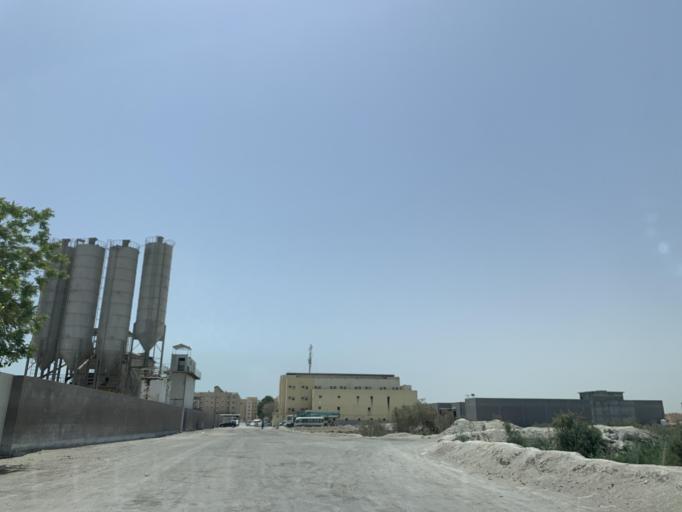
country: BH
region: Northern
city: Sitrah
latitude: 26.1472
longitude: 50.5941
